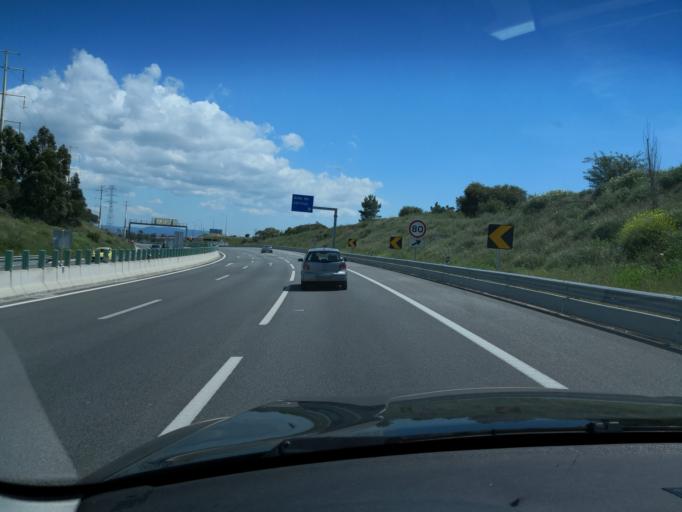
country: PT
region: Setubal
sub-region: Almada
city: Sobreda
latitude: 38.6401
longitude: -9.2013
